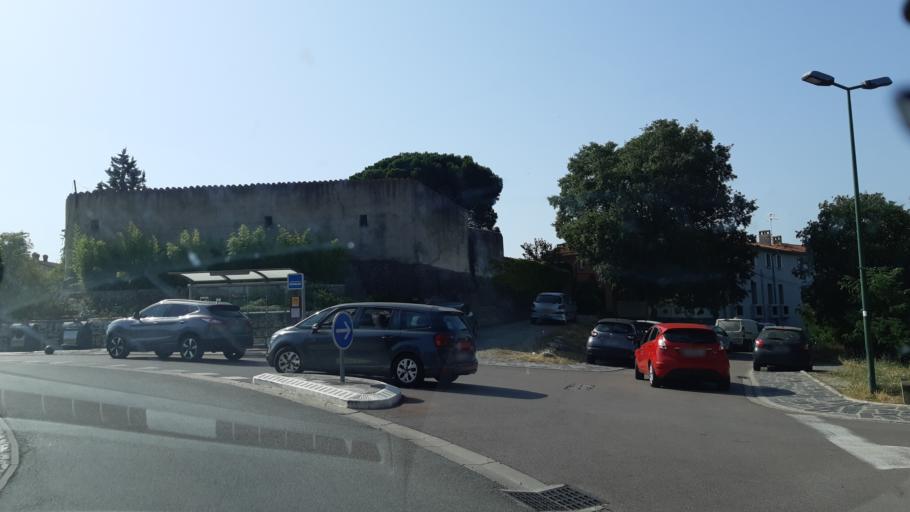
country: FR
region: Languedoc-Roussillon
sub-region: Departement des Pyrenees-Orientales
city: Sant Joan de Pladecorts
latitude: 42.5114
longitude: 2.7900
